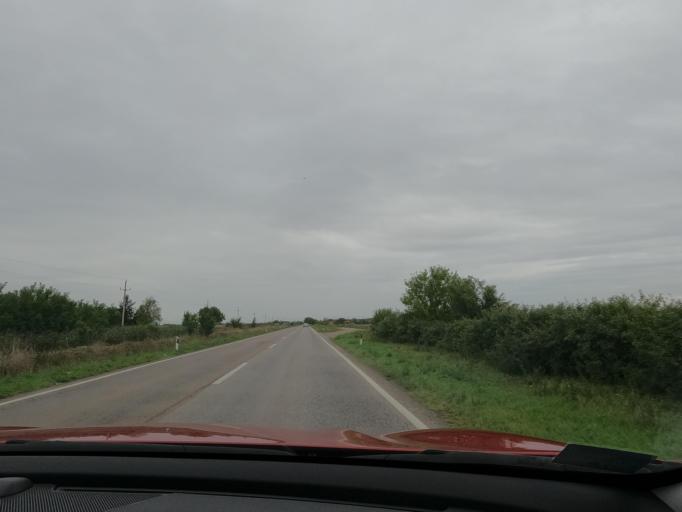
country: RS
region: Autonomna Pokrajina Vojvodina
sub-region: Severnobanatski Okrug
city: Kikinda
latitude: 45.7745
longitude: 20.4266
